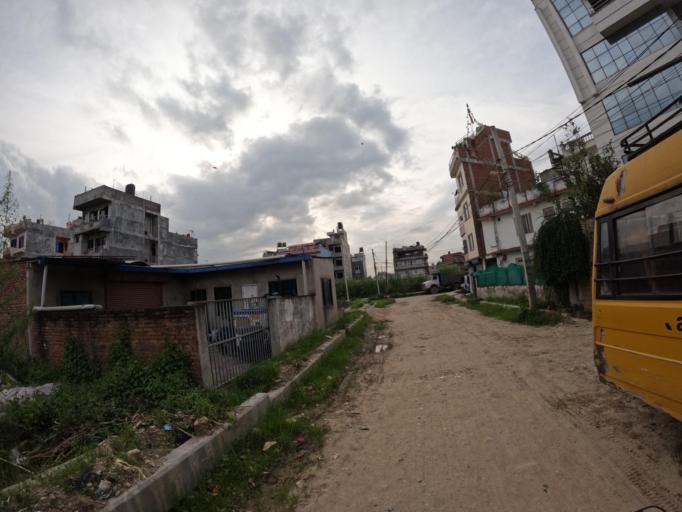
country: NP
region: Central Region
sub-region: Bagmati Zone
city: Bhaktapur
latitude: 27.6813
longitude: 85.3914
